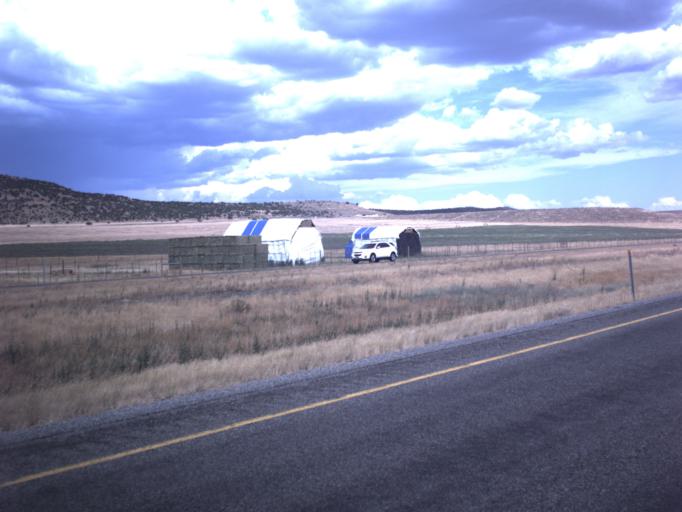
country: US
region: Idaho
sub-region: Oneida County
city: Malad City
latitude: 41.9777
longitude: -112.7954
